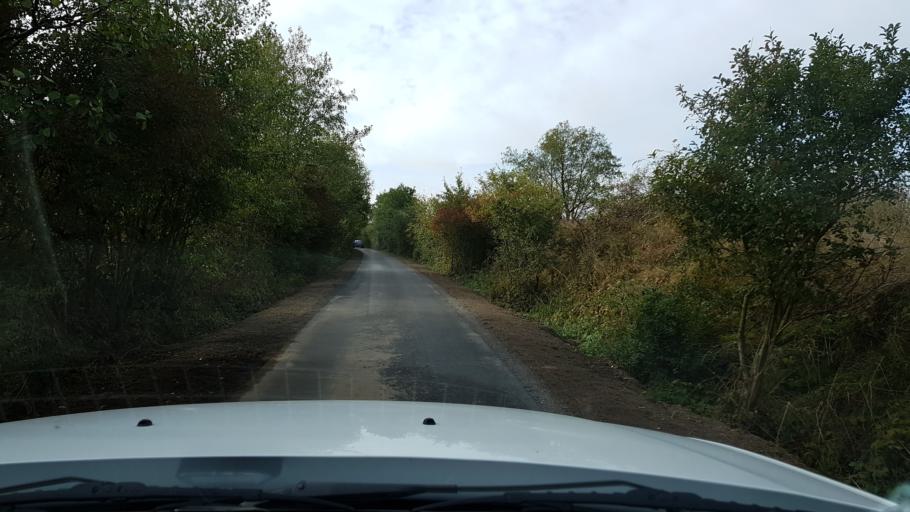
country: PL
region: West Pomeranian Voivodeship
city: Trzcinsko Zdroj
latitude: 52.9494
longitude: 14.5769
